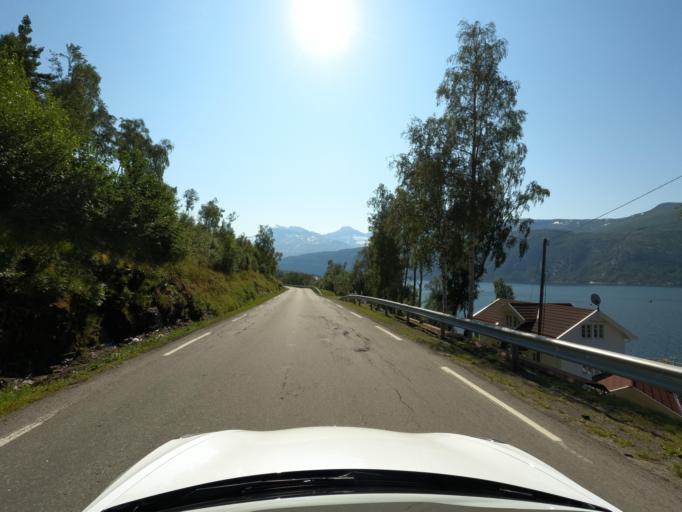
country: NO
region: Nordland
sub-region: Narvik
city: Narvik
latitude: 68.3426
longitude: 17.2779
